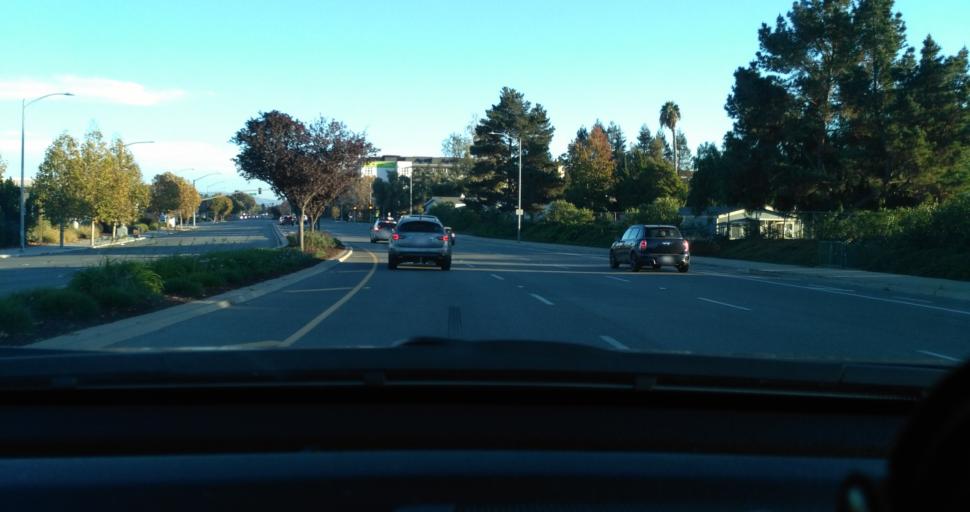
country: US
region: California
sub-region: Santa Clara County
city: Milpitas
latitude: 37.4175
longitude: -121.9577
